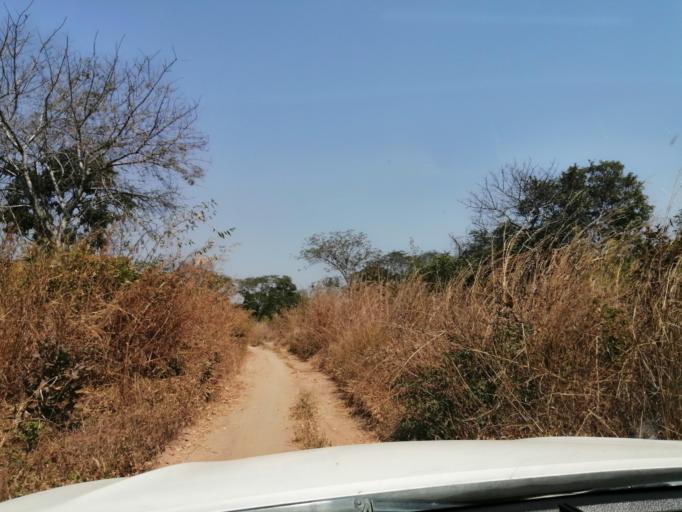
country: ZM
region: Eastern
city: Nyimba
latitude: -14.3074
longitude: 30.0525
